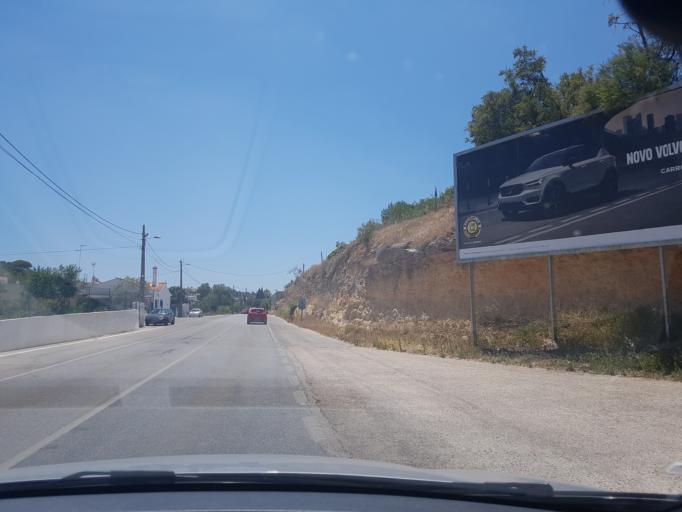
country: PT
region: Faro
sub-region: Lagoa
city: Carvoeiro
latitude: 37.1087
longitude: -8.4615
